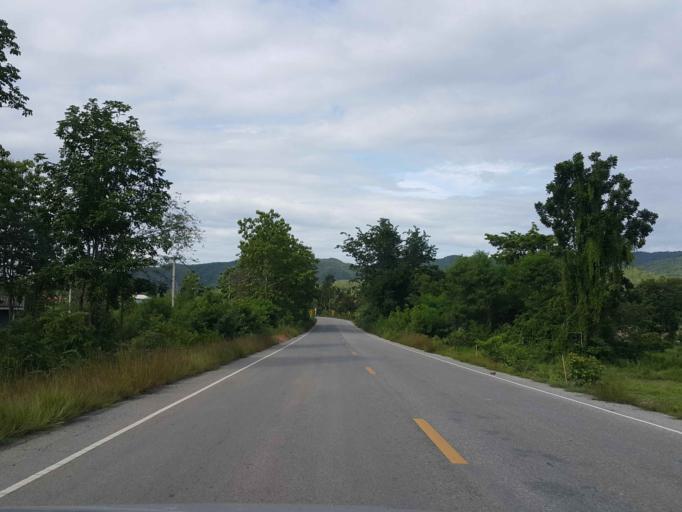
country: TH
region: Sukhothai
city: Thung Saliam
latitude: 17.2331
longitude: 99.5132
